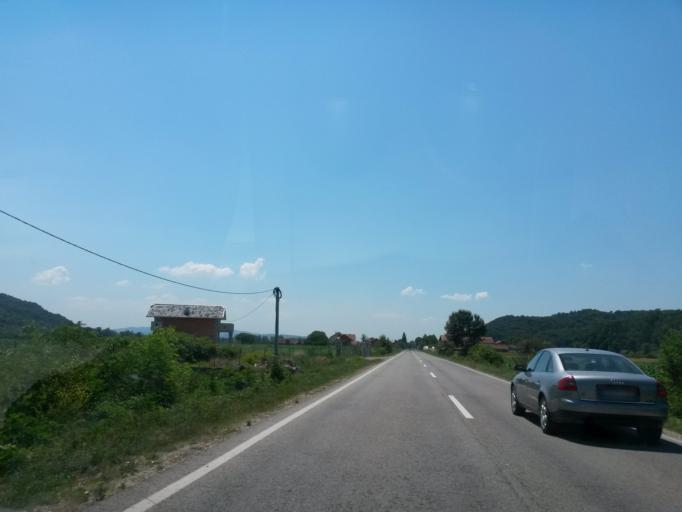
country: BA
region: Federation of Bosnia and Herzegovina
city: Lukavica
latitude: 44.8927
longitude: 18.0949
